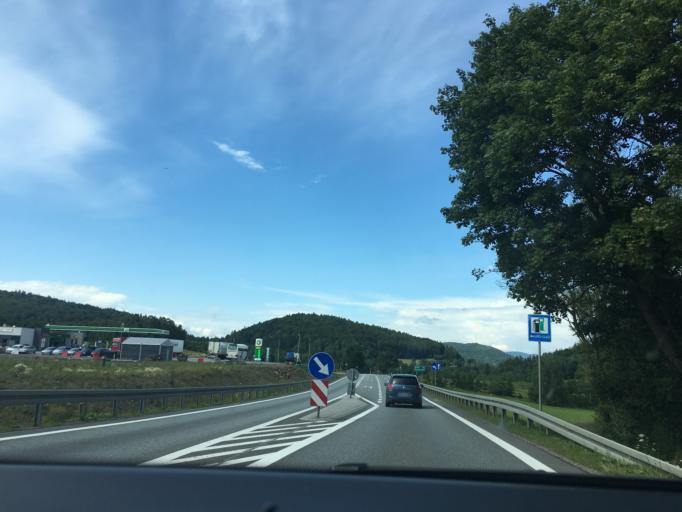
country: PL
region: Subcarpathian Voivodeship
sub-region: Powiat krosnienski
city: Jasliska
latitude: 49.4380
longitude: 21.6908
